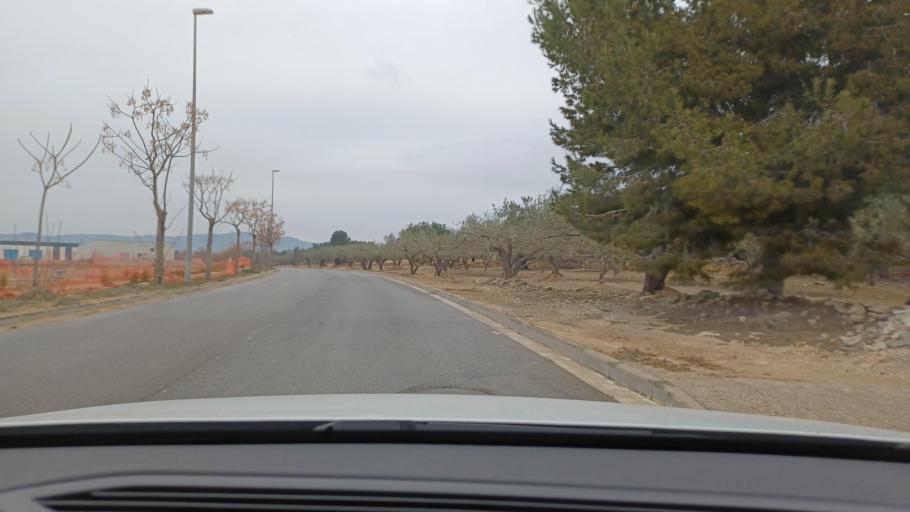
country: ES
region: Catalonia
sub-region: Provincia de Tarragona
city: Amposta
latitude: 40.7654
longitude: 0.5987
